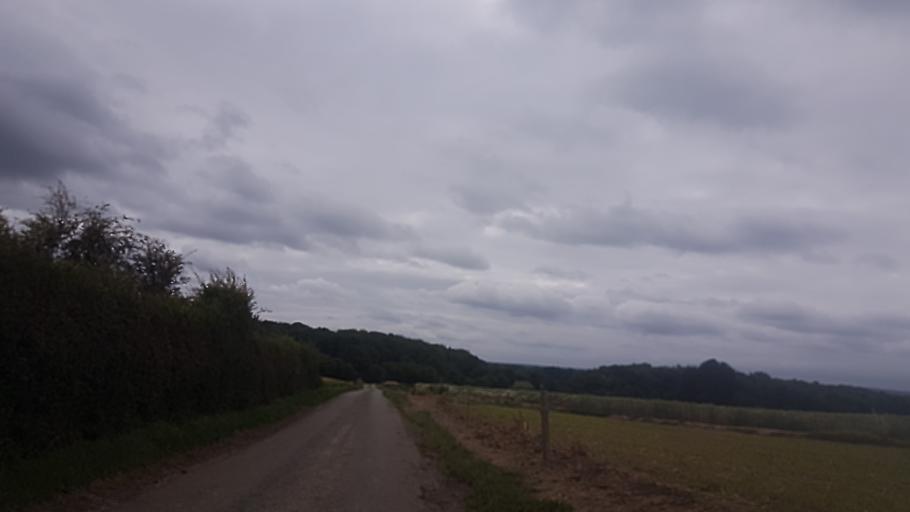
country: BE
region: Wallonia
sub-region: Province de Namur
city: Philippeville
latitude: 50.1054
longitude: 4.5830
